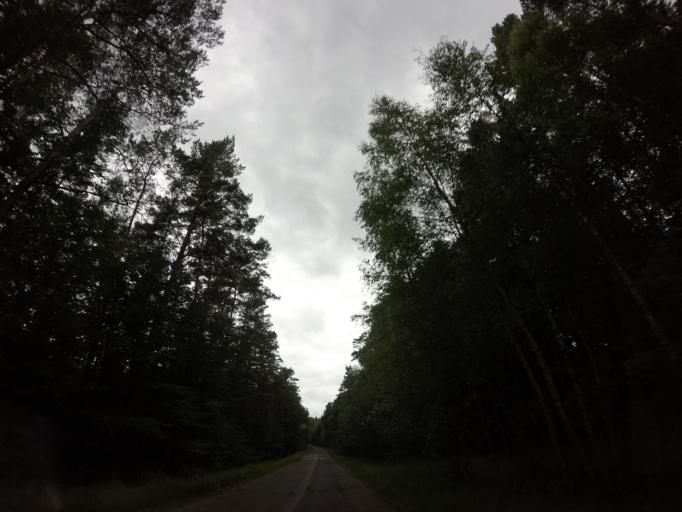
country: PL
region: West Pomeranian Voivodeship
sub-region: Powiat stargardzki
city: Insko
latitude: 53.4626
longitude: 15.6692
